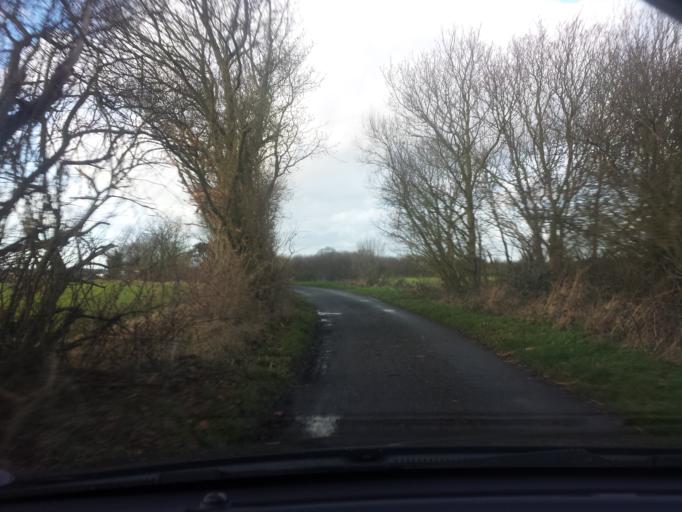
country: GB
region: England
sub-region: Essex
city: Manningtree
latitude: 51.9005
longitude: 1.0480
